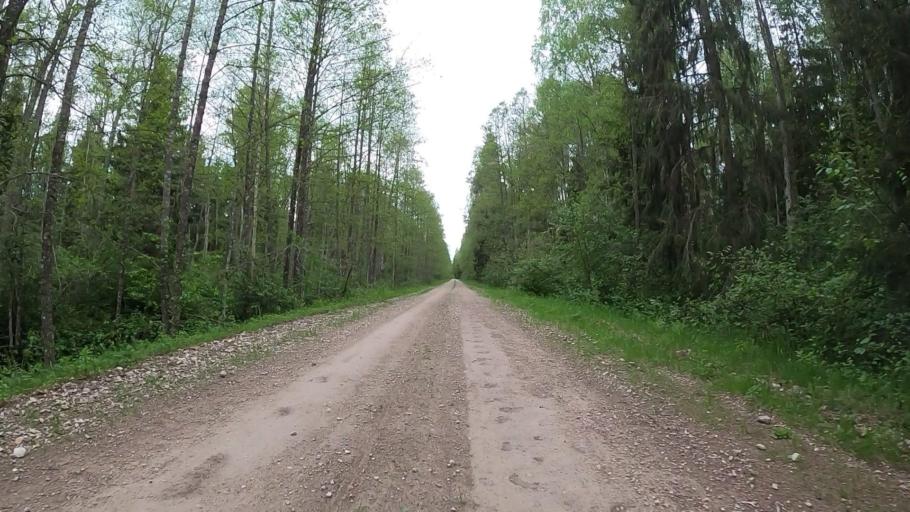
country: LV
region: Ozolnieku
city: Ozolnieki
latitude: 56.8075
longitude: 23.7865
